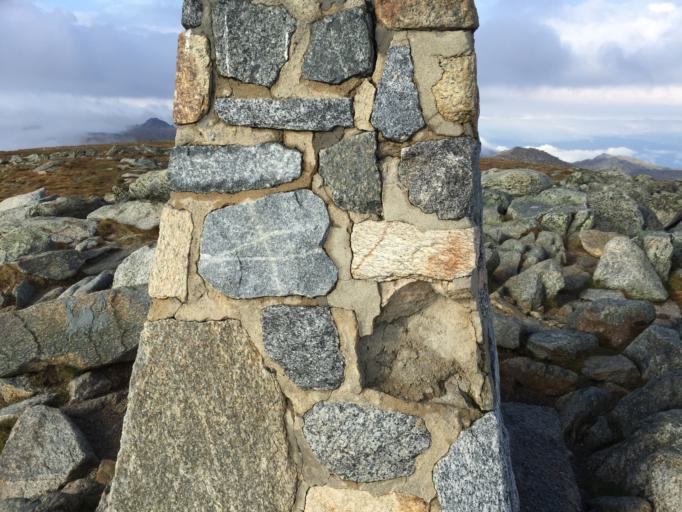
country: AU
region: New South Wales
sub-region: Snowy River
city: Jindabyne
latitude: -36.4558
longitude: 148.2635
